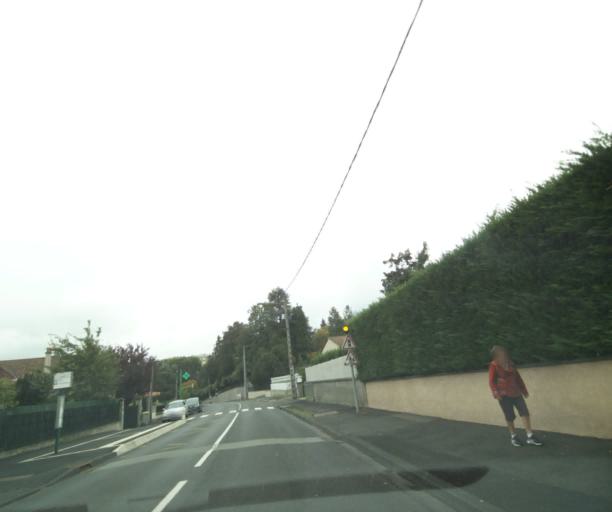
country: FR
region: Auvergne
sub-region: Departement du Puy-de-Dome
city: Durtol
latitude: 45.7914
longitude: 3.0535
